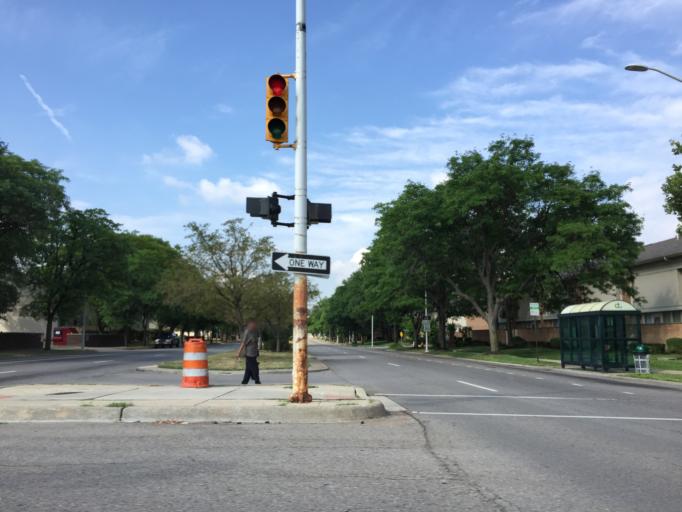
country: US
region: Michigan
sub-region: Wayne County
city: Detroit
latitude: 42.3414
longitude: -83.0249
